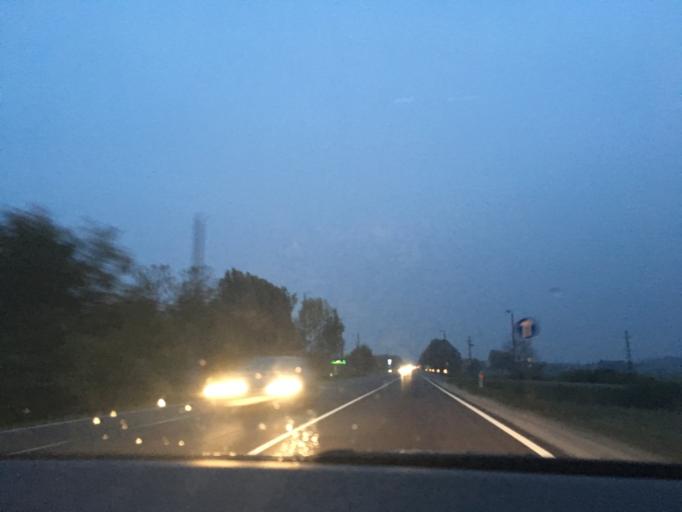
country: HU
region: Pest
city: Albertirsa
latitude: 47.2618
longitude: 19.5965
